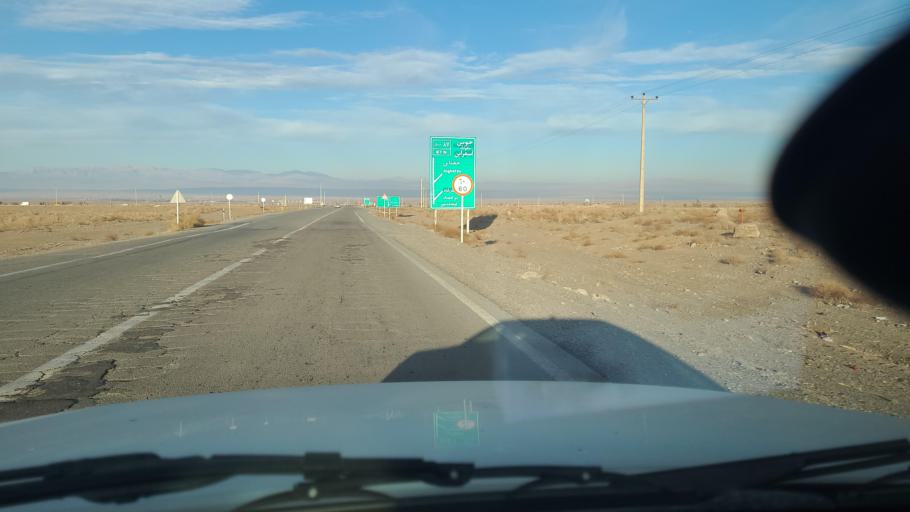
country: IR
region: Razavi Khorasan
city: Neqab
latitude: 36.5091
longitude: 57.5372
